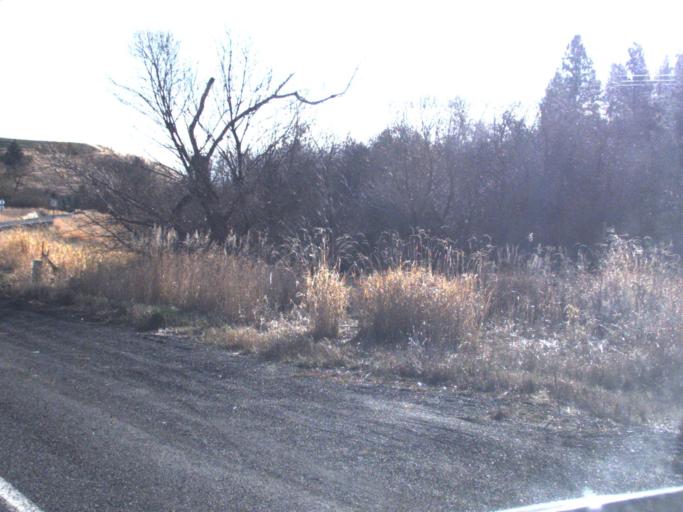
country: US
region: Washington
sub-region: Whitman County
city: Colfax
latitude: 46.7429
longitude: -117.3328
